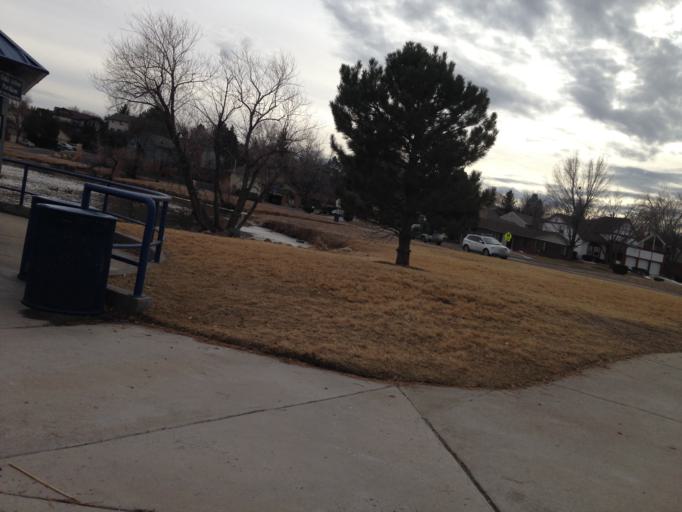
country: US
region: Colorado
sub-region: Adams County
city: Westminster
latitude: 39.8442
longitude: -105.0708
